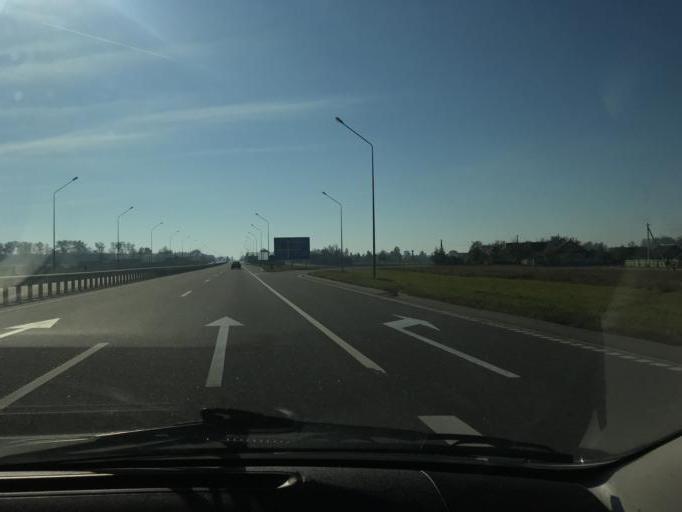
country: BY
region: Minsk
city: Slutsk
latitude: 53.2270
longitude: 27.5504
